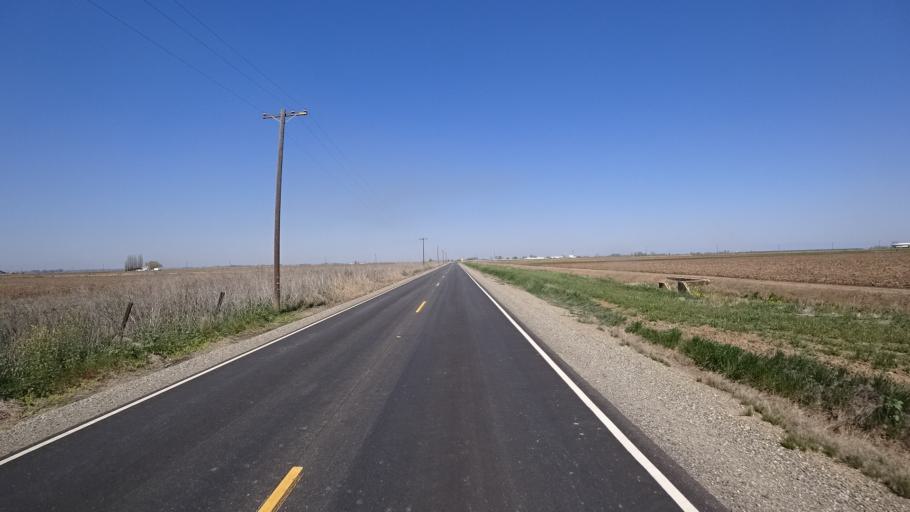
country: US
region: California
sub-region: Glenn County
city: Willows
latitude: 39.4909
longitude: -122.1368
